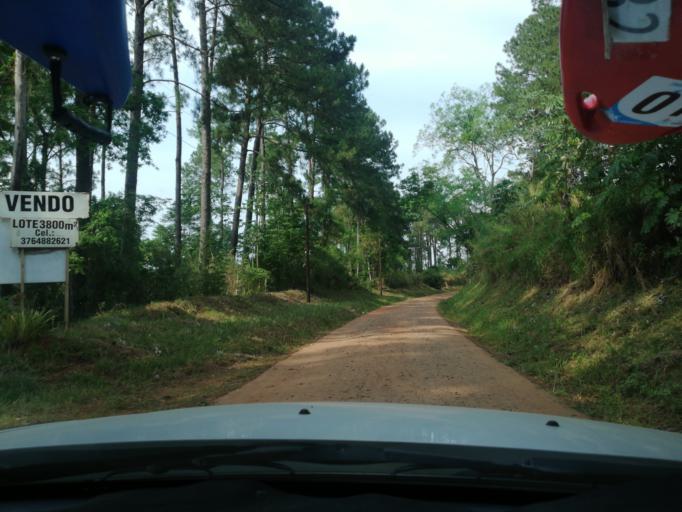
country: AR
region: Misiones
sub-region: Departamento de San Ignacio
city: San Ignacio
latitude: -27.2929
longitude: -55.5642
